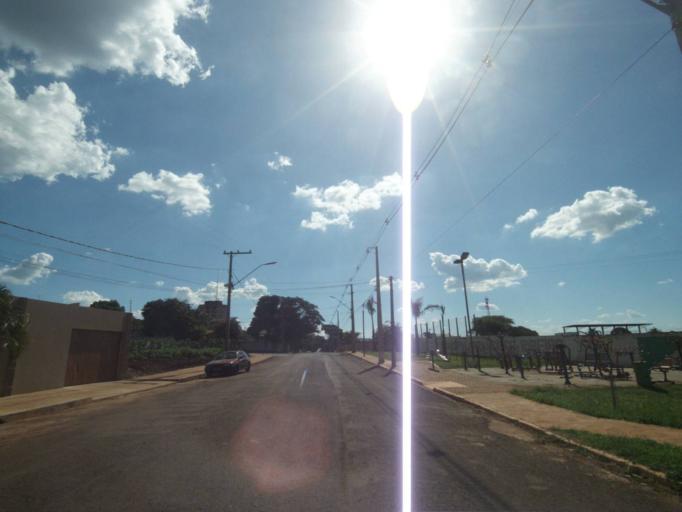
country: BR
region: Parana
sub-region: Sertanopolis
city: Sertanopolis
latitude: -23.0401
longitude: -50.8130
